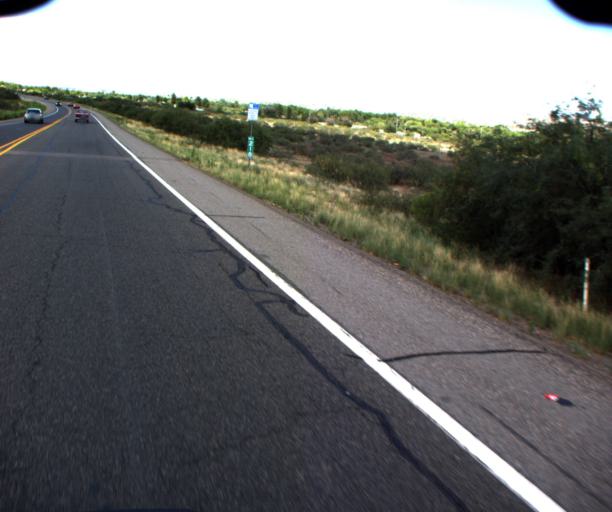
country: US
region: Arizona
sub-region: Yavapai County
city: Camp Verde
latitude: 34.5871
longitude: -111.8872
